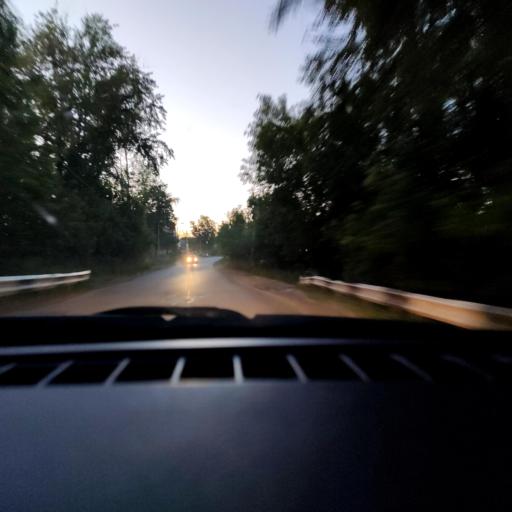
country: RU
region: Perm
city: Polazna
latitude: 58.1255
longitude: 56.3974
